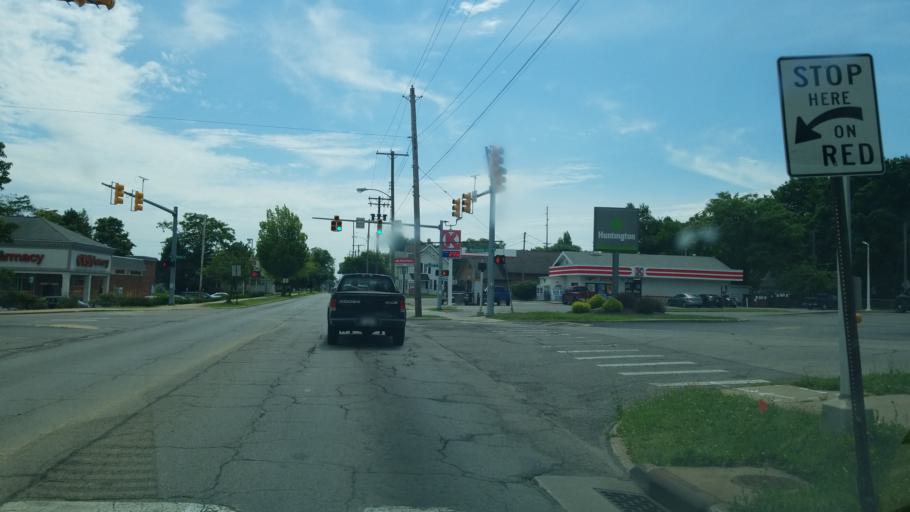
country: US
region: Ohio
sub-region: Ashland County
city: Ashland
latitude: 40.8681
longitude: -82.3082
